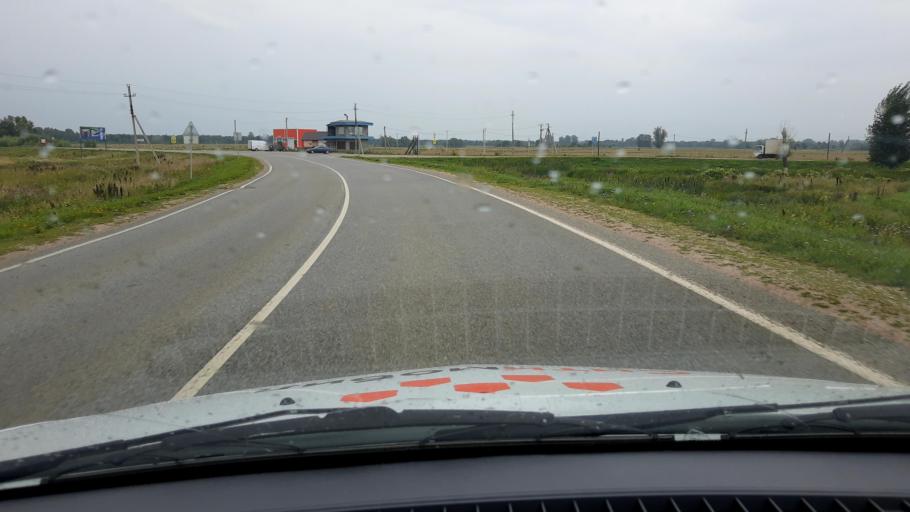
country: RU
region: Bashkortostan
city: Krasnaya Gorka
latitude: 55.1783
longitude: 56.6677
